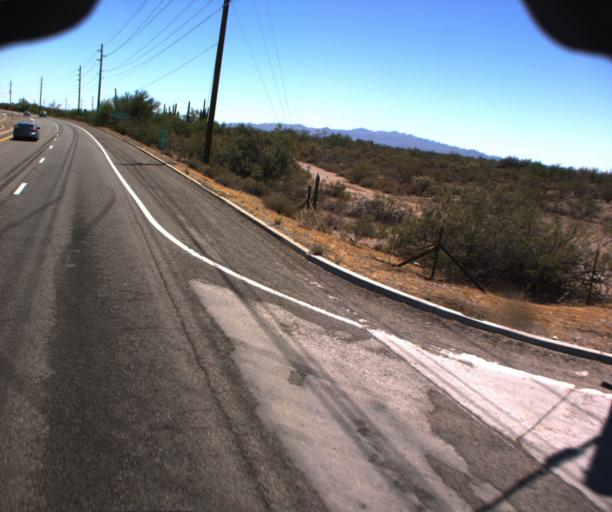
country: US
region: Arizona
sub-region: Maricopa County
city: Wickenburg
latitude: 33.8545
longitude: -112.6235
